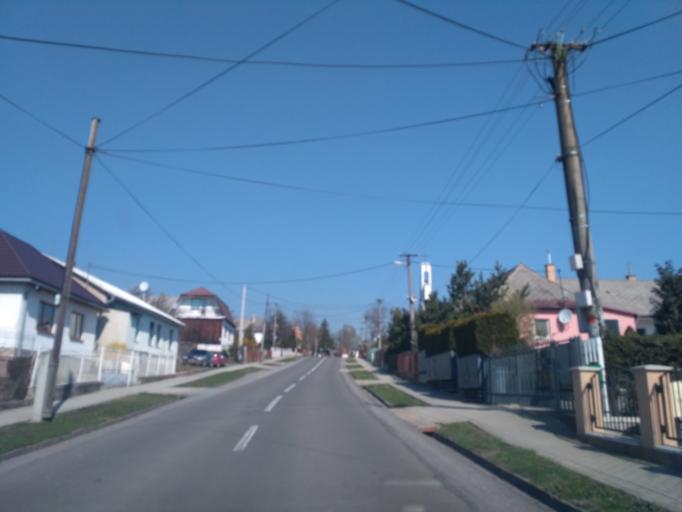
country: SK
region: Kosicky
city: Secovce
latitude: 48.7573
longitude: 21.6424
